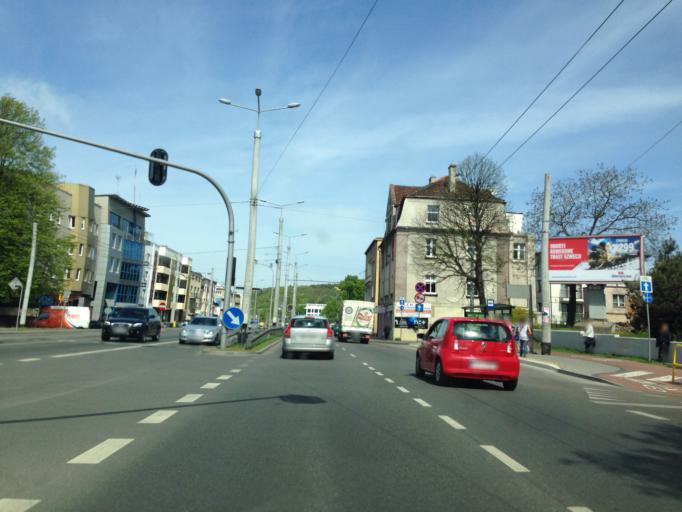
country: PL
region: Pomeranian Voivodeship
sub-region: Sopot
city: Sopot
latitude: 54.4762
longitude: 18.5533
